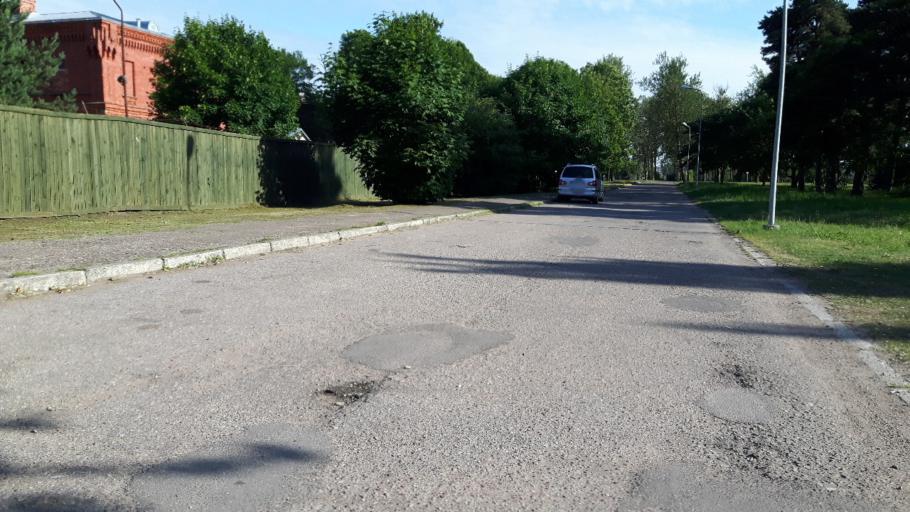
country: LV
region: Liepaja
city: Vec-Liepaja
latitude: 56.5466
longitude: 21.0202
